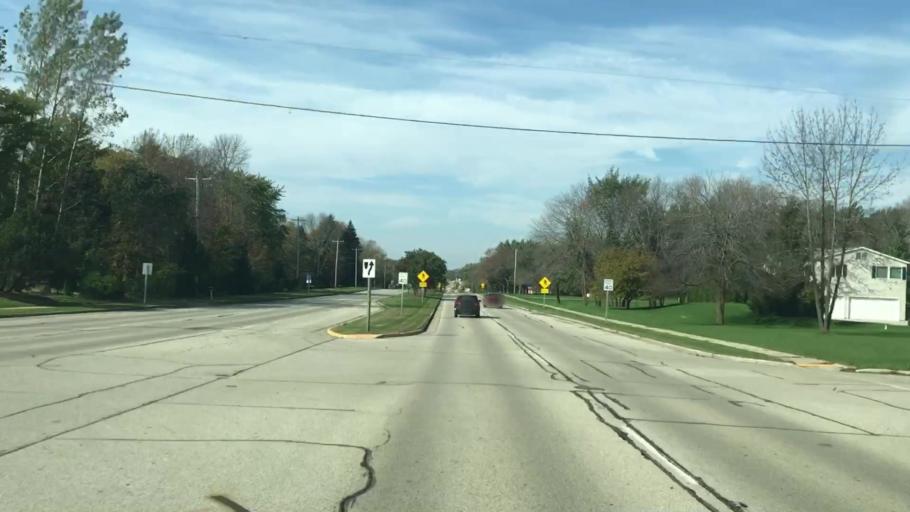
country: US
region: Wisconsin
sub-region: Ozaukee County
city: Thiensville
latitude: 43.2215
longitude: -87.9339
